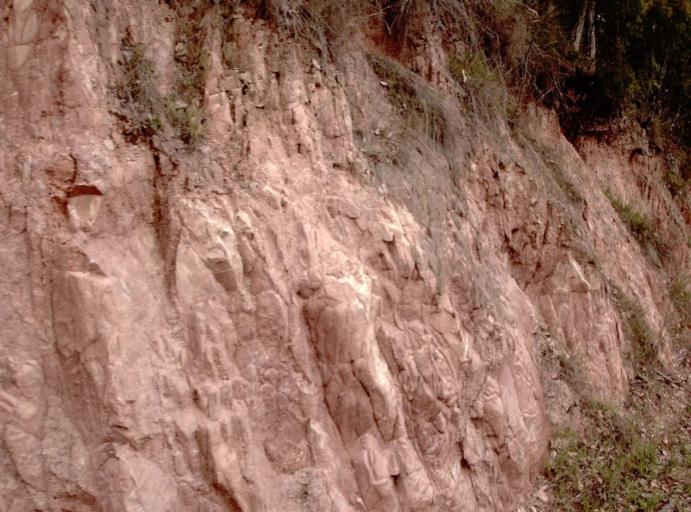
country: AU
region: Victoria
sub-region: East Gippsland
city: Bairnsdale
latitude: -37.7180
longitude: 147.5940
